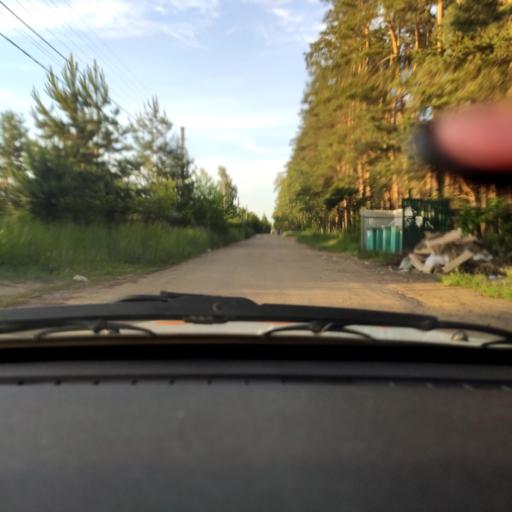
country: RU
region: Voronezj
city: Podgornoye
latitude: 51.8341
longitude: 39.1963
